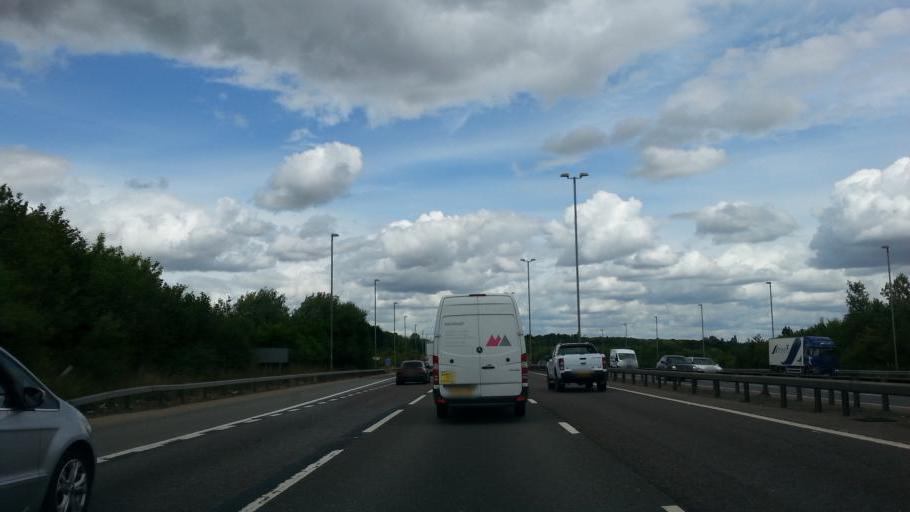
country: GB
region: England
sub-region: Essex
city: Little Hallingbury
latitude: 51.8626
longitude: 0.1919
